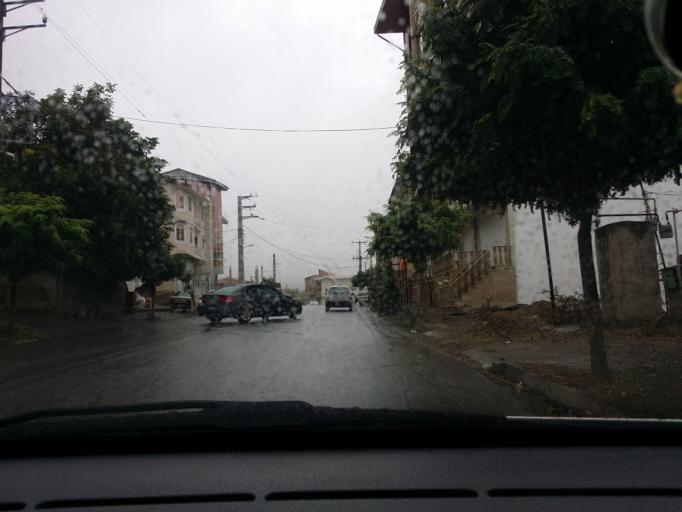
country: IR
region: Mazandaran
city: Chalus
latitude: 36.5251
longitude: 51.2325
